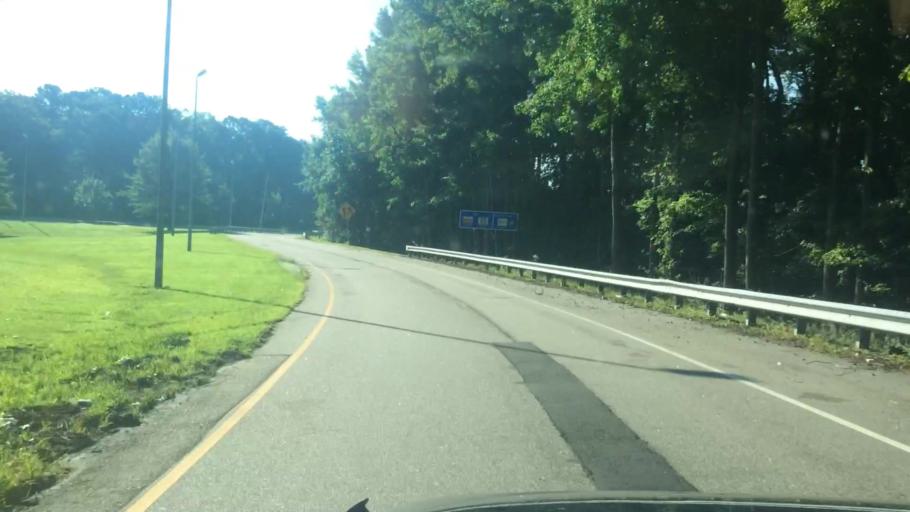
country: US
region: Virginia
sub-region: City of Newport News
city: Newport News
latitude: 37.0889
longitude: -76.4611
